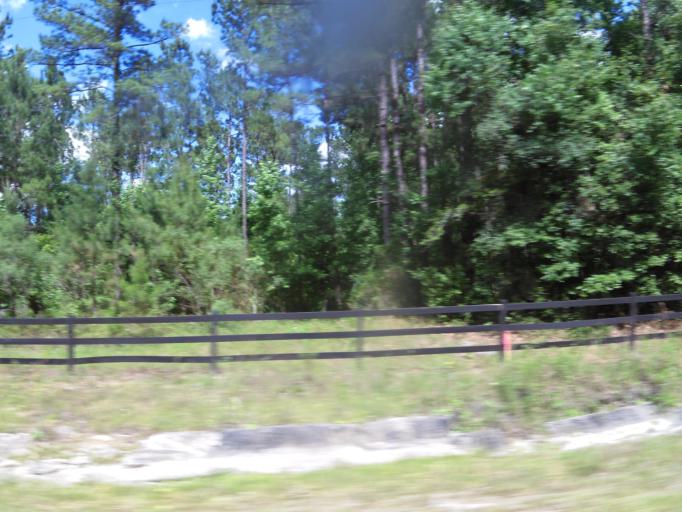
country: US
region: Florida
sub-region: Clay County
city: Asbury Lake
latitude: 29.9027
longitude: -81.8765
